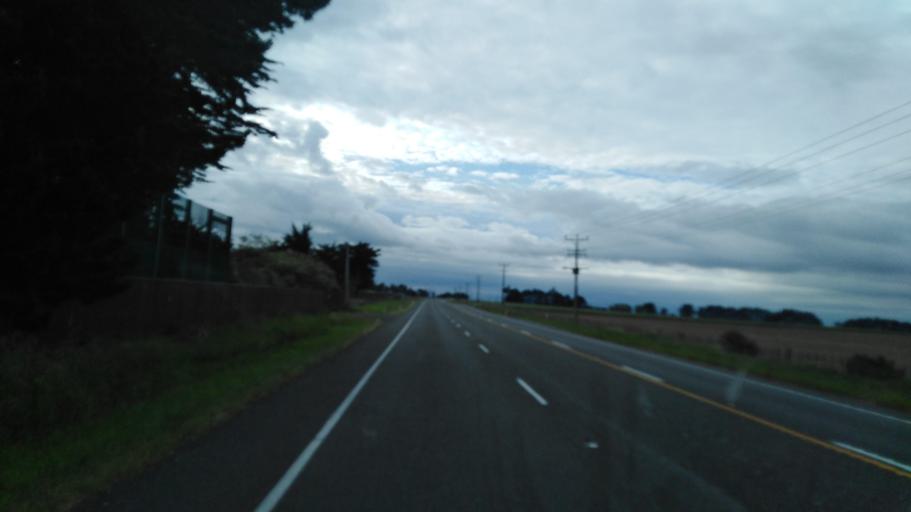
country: NZ
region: Manawatu-Wanganui
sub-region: Rangitikei District
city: Bulls
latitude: -40.1301
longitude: 175.3589
